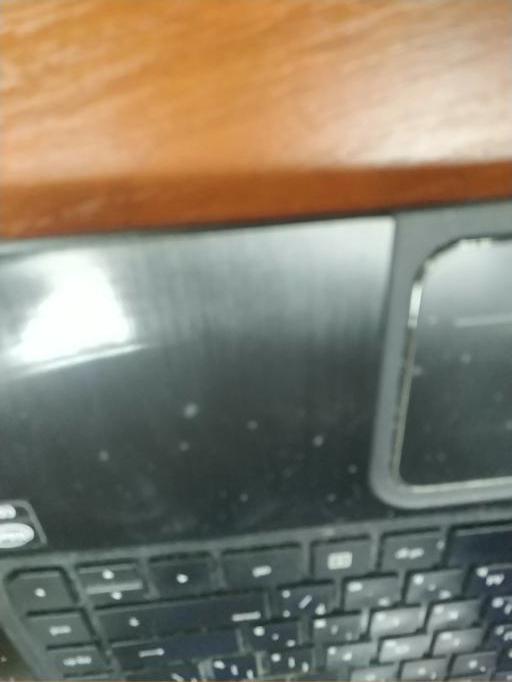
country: RU
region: Moscow
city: Lianozovo
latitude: 55.9088
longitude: 37.5866
